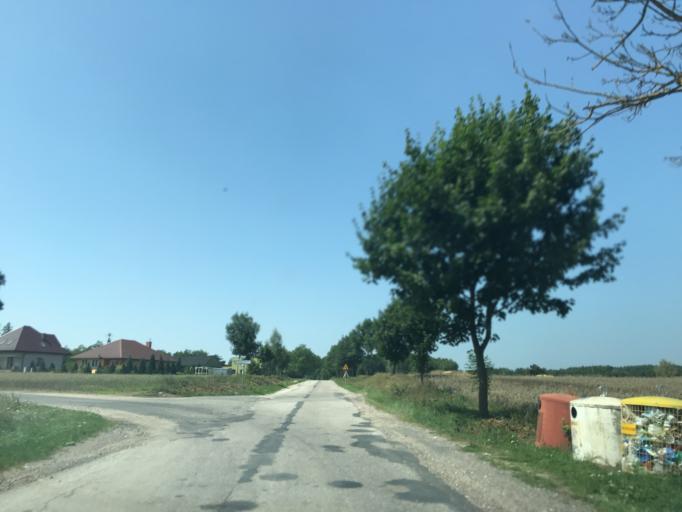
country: PL
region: Kujawsko-Pomorskie
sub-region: Powiat lipnowski
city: Chrostkowo
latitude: 52.9892
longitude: 19.2921
